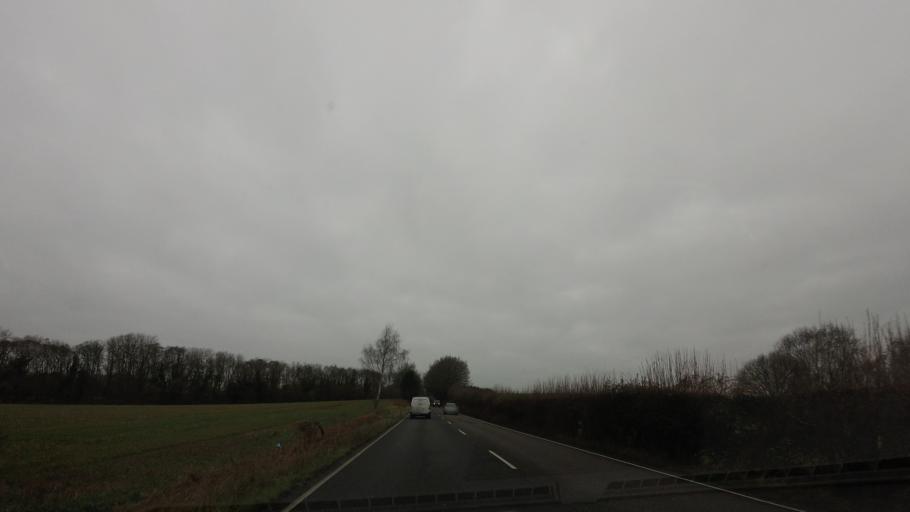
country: GB
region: England
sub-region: East Sussex
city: Battle
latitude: 50.9333
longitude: 0.5220
